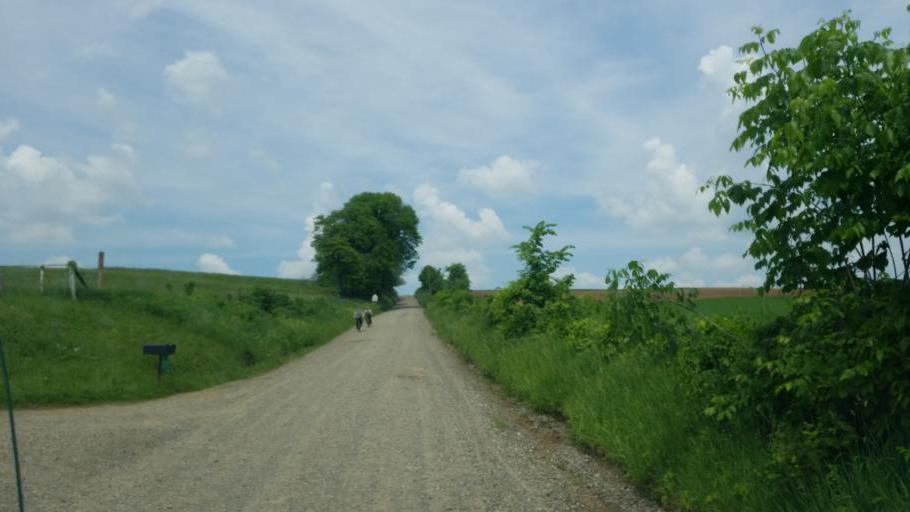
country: US
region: Ohio
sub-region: Holmes County
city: Millersburg
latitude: 40.4868
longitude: -81.7945
